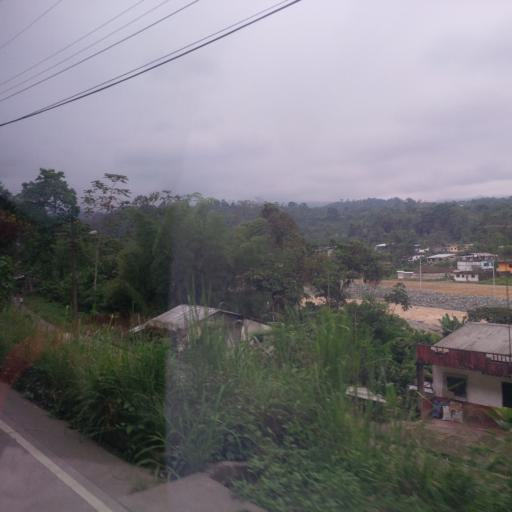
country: EC
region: Chimborazo
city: Alausi
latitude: -2.2018
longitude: -79.1298
